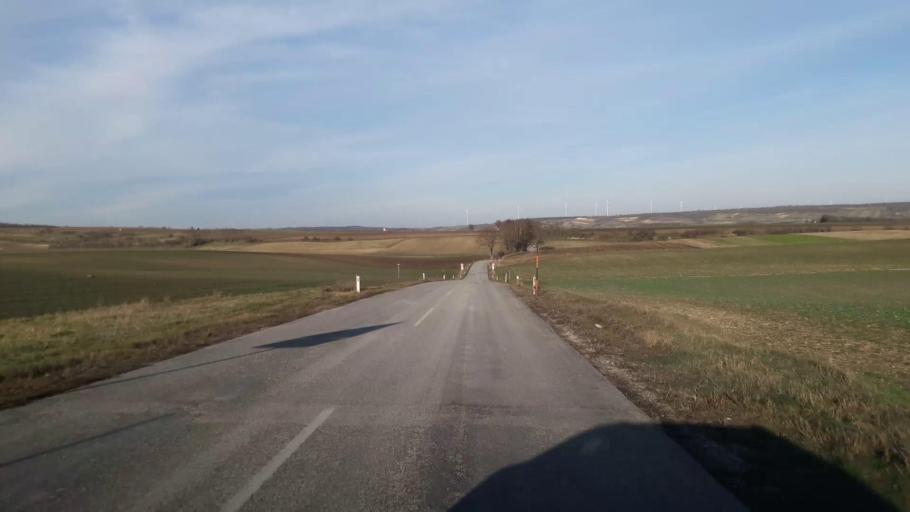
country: AT
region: Lower Austria
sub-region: Politischer Bezirk Ganserndorf
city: Auersthal
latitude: 48.3859
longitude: 16.6308
